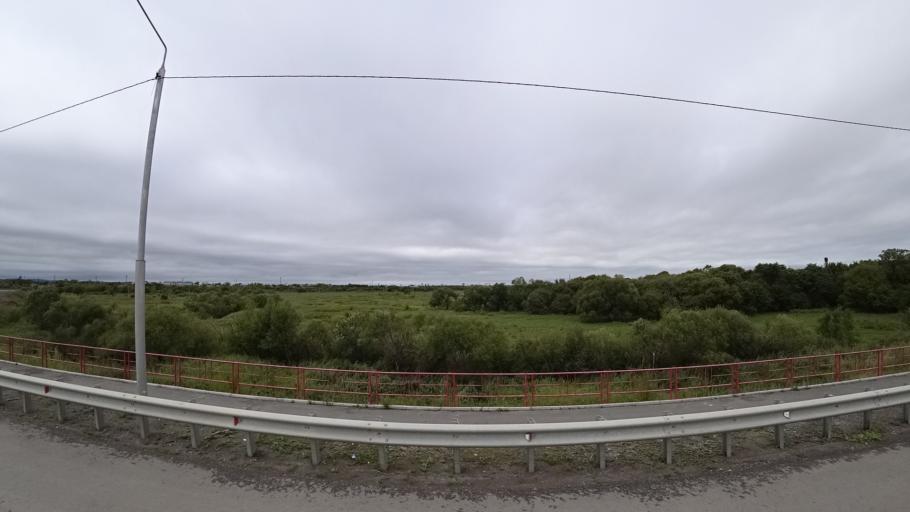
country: RU
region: Primorskiy
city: Monastyrishche
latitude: 44.1956
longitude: 132.4442
